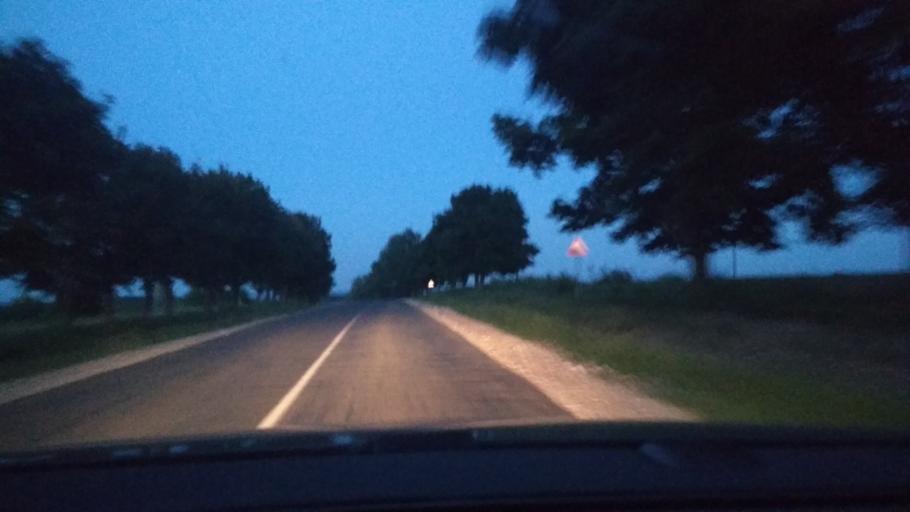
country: MD
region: Nisporeni
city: Nisporeni
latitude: 47.1571
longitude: 28.1840
